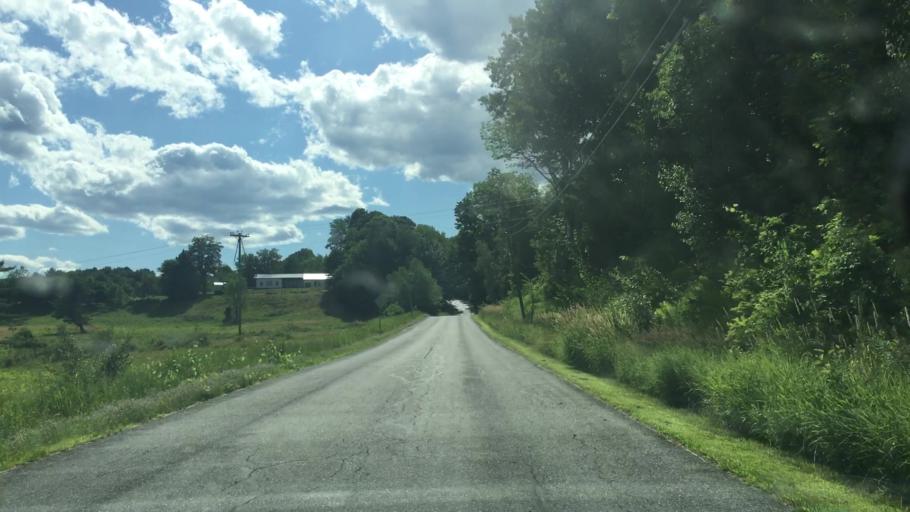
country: US
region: Maine
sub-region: Franklin County
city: Farmington
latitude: 44.6447
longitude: -70.1881
